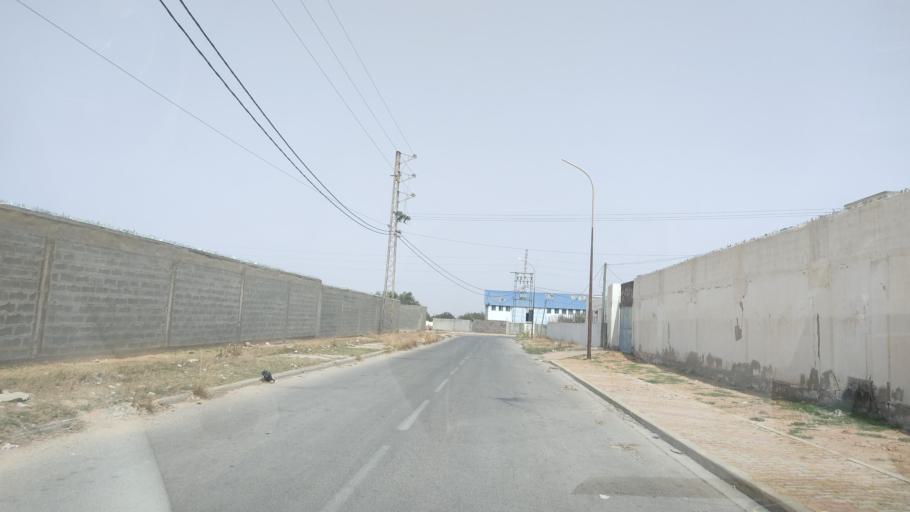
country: TN
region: Al Mahdiyah
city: El Jem
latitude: 35.1303
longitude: 10.7364
